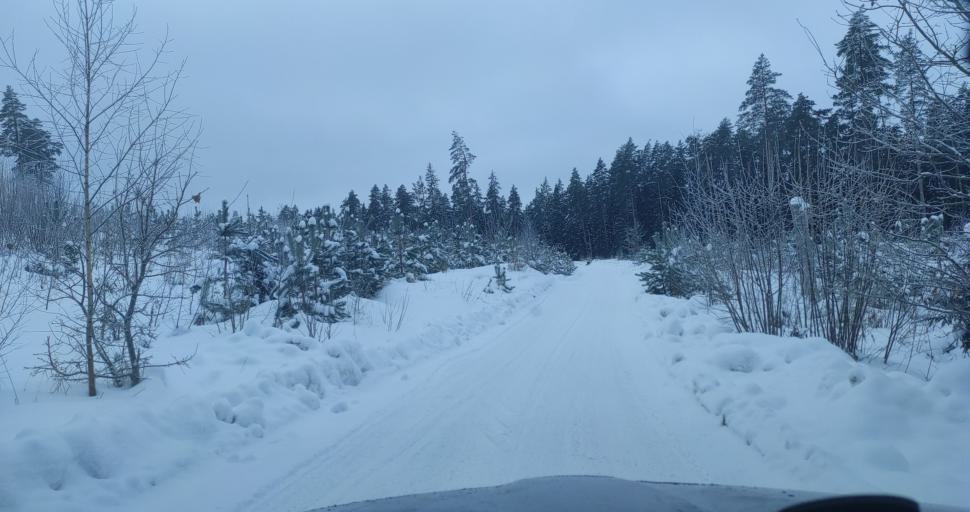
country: LV
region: Plavinu
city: Plavinas
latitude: 56.6562
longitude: 25.7460
